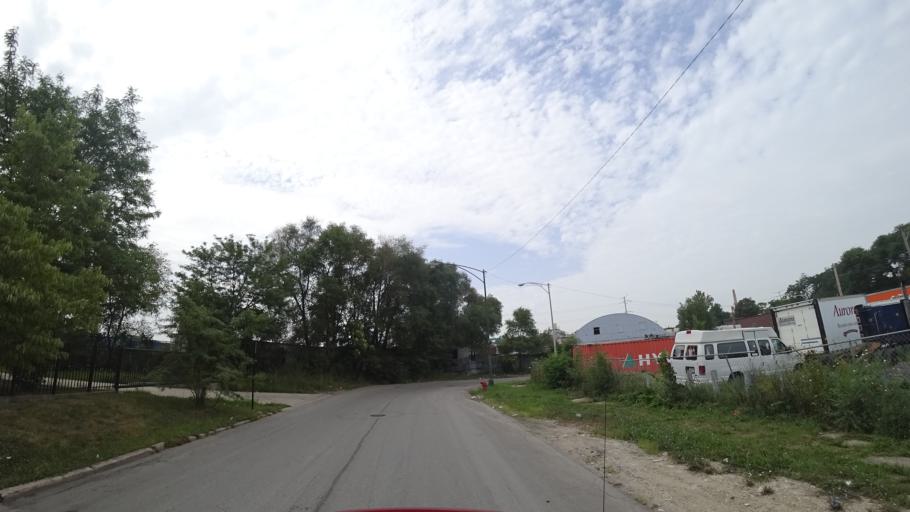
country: US
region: Illinois
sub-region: Cook County
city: Cicero
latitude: 41.8356
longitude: -87.7146
